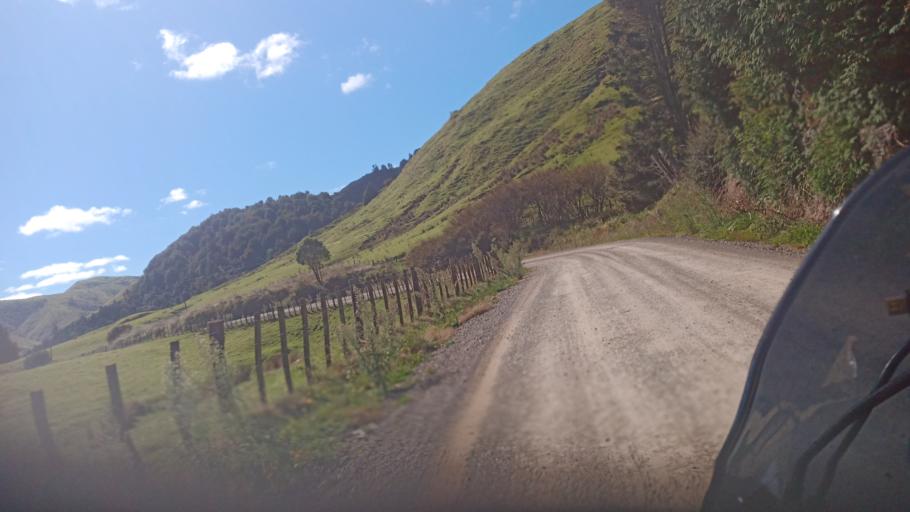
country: NZ
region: Bay of Plenty
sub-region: Opotiki District
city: Opotiki
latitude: -38.3053
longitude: 177.5616
